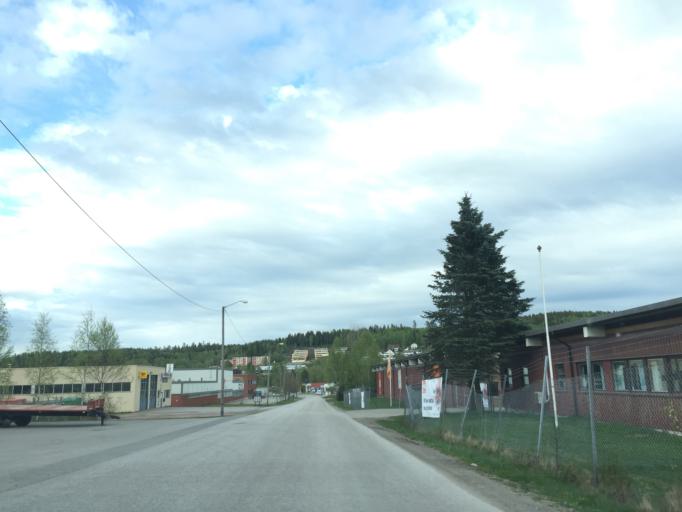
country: NO
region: Hedmark
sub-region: Kongsvinger
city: Kongsvinger
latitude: 60.1702
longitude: 12.0182
